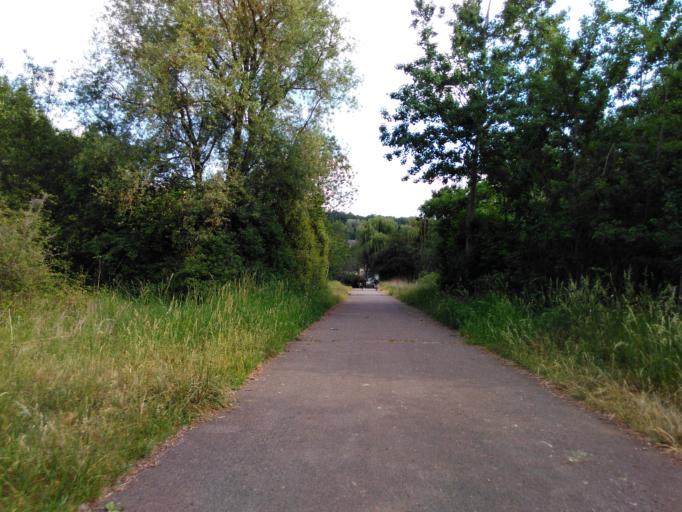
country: LU
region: Luxembourg
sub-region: Canton d'Esch-sur-Alzette
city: Schifflange
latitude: 49.5089
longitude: 6.0028
